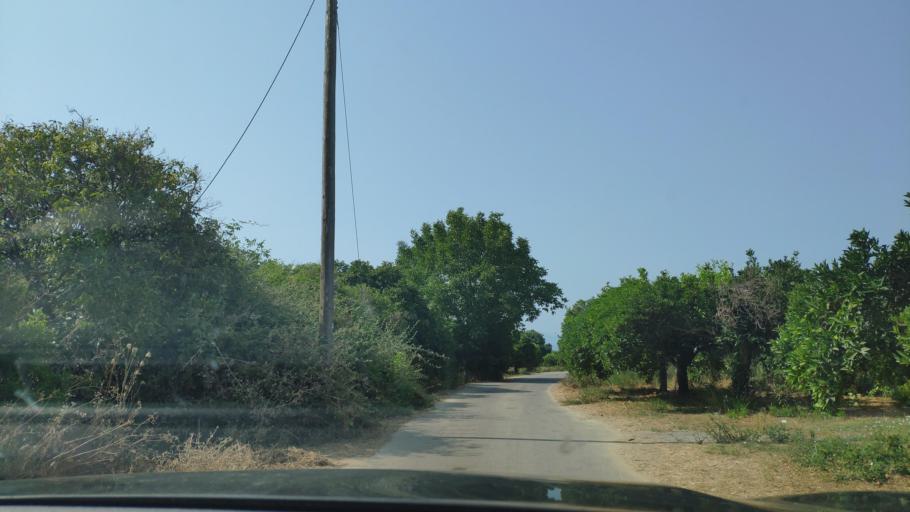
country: GR
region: Epirus
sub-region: Nomos Artas
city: Kompoti
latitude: 39.0720
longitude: 21.0817
